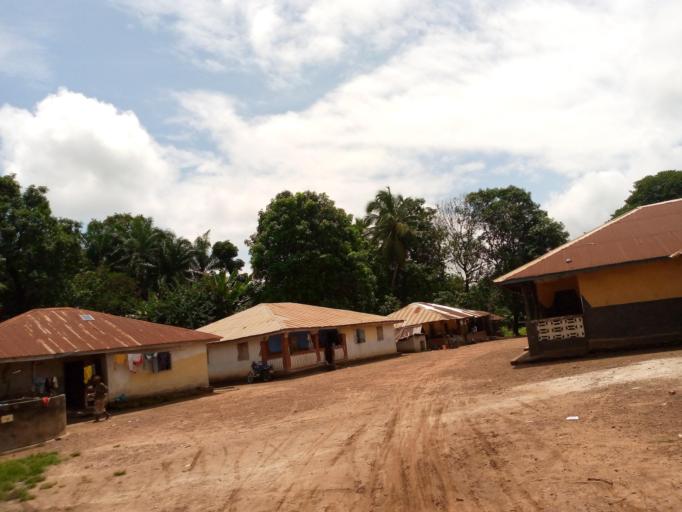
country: SL
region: Northern Province
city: Magburaka
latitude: 8.7277
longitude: -11.9220
